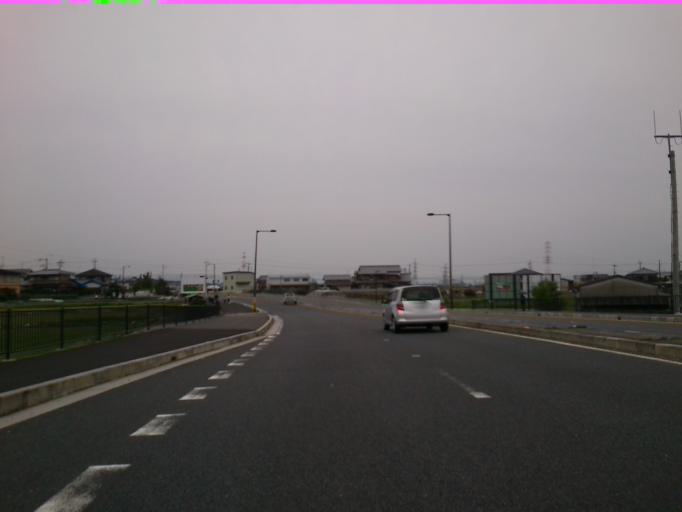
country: JP
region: Kyoto
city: Tanabe
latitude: 34.8220
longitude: 135.7594
